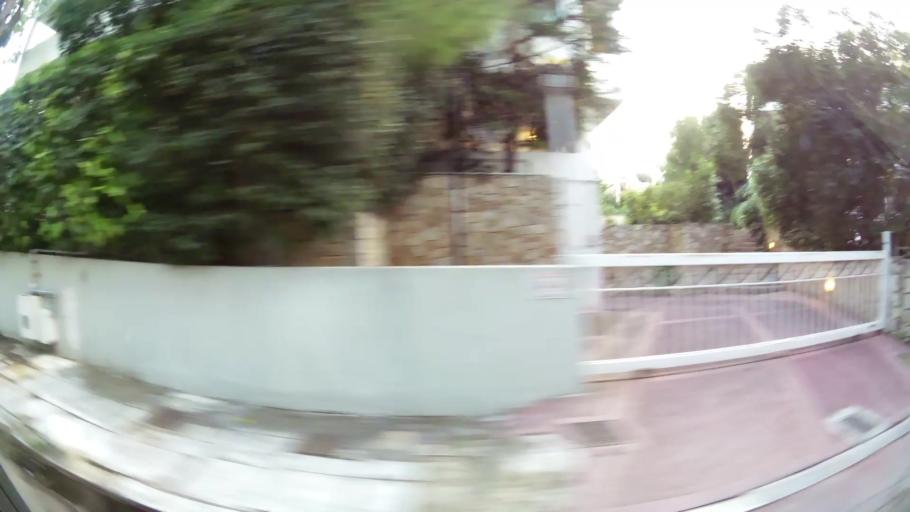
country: GR
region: Attica
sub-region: Nomarchia Athinas
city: Filothei
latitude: 38.0204
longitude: 23.7794
